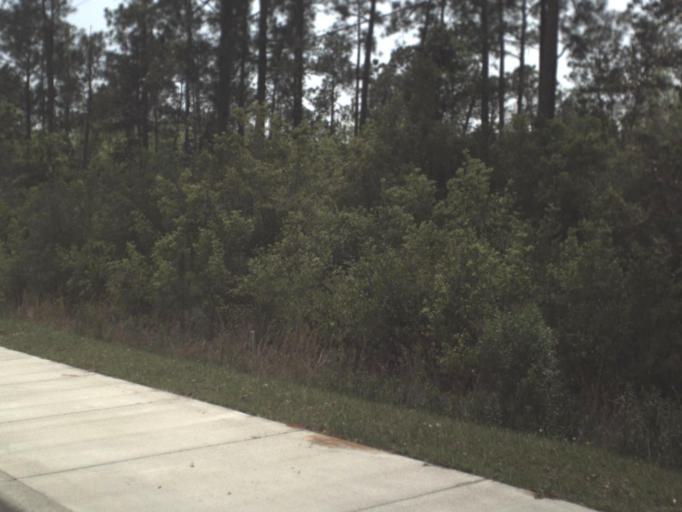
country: US
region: Florida
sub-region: Santa Rosa County
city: Bagdad
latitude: 30.5558
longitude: -87.0872
